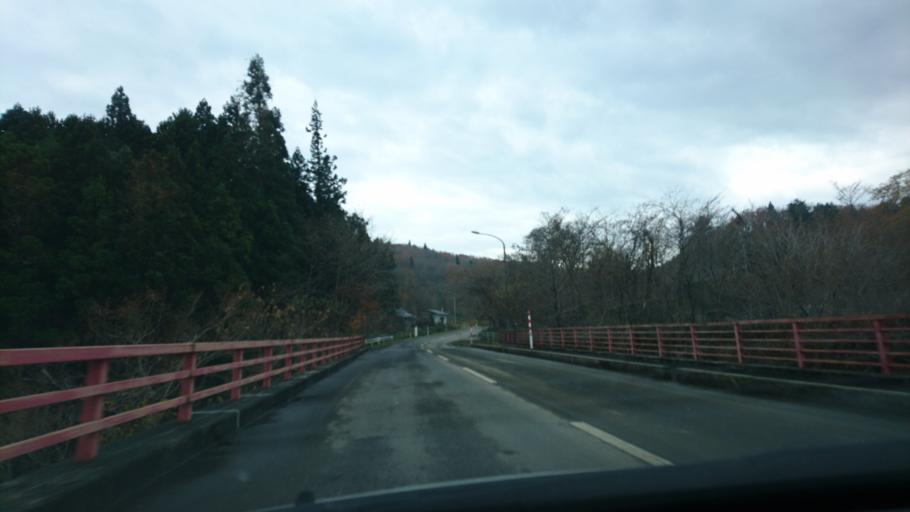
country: JP
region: Iwate
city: Ichinoseki
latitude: 38.9732
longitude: 140.9416
